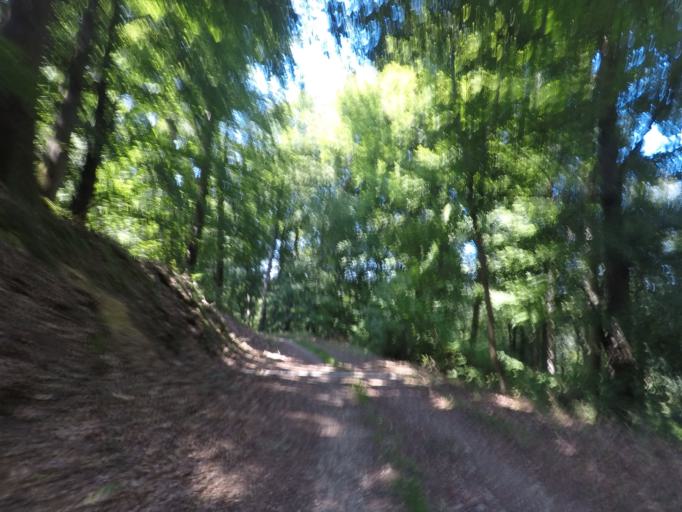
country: LU
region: Luxembourg
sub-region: Canton de Capellen
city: Kopstal
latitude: 49.6563
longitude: 6.0708
